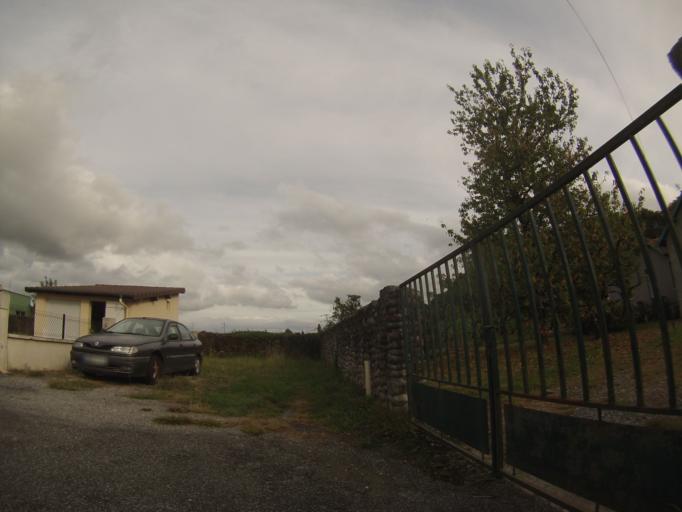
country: FR
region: Aquitaine
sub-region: Departement des Pyrenees-Atlantiques
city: Gelos
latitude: 43.2800
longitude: -0.3690
